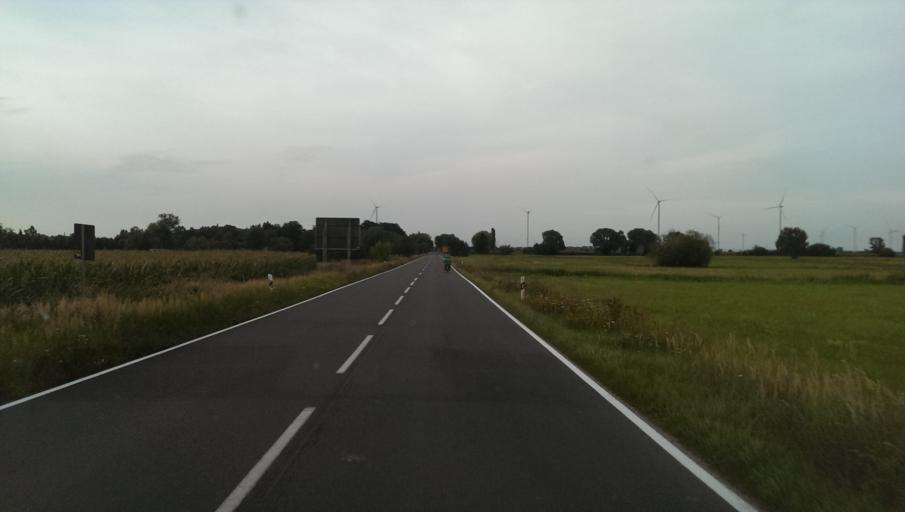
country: DE
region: Saxony-Anhalt
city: Kemberg
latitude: 51.7662
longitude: 12.6396
